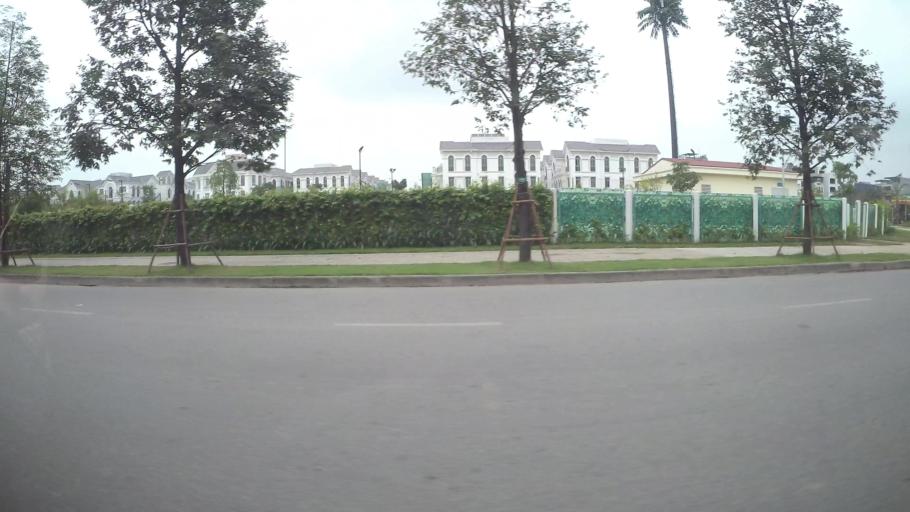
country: VN
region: Ha Noi
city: Trau Quy
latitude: 21.0519
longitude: 105.9073
